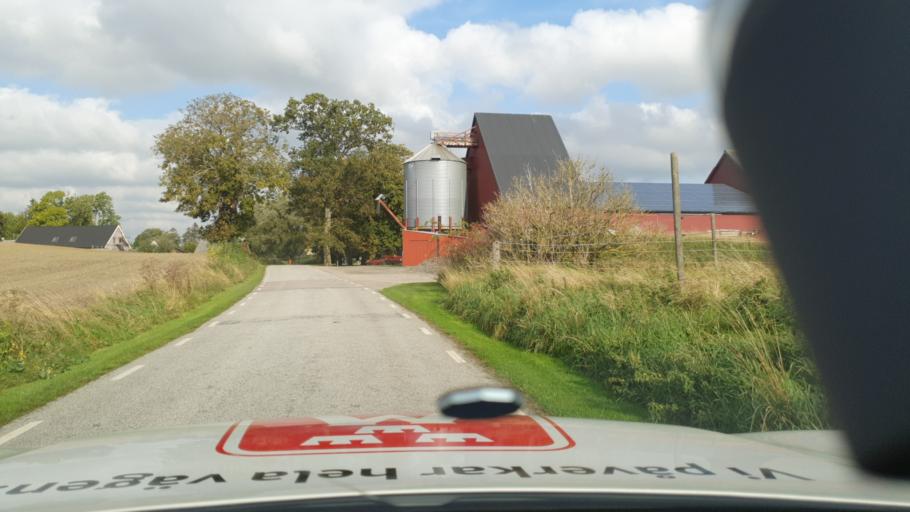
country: SE
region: Skane
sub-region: Svedala Kommun
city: Svedala
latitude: 55.4951
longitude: 13.1856
